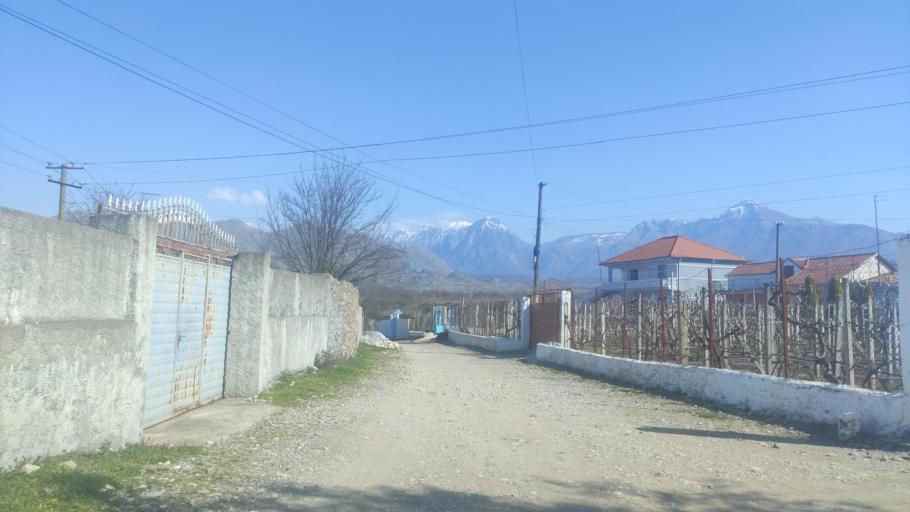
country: AL
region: Shkoder
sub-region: Rrethi i Malesia e Madhe
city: Grude-Fushe
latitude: 42.1713
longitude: 19.4842
